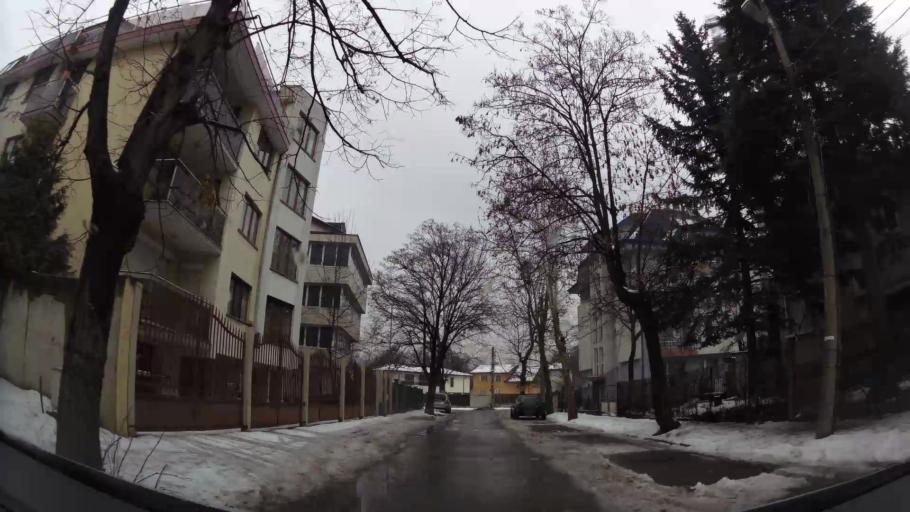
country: BG
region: Sofia-Capital
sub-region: Stolichna Obshtina
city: Sofia
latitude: 42.6753
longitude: 23.2664
